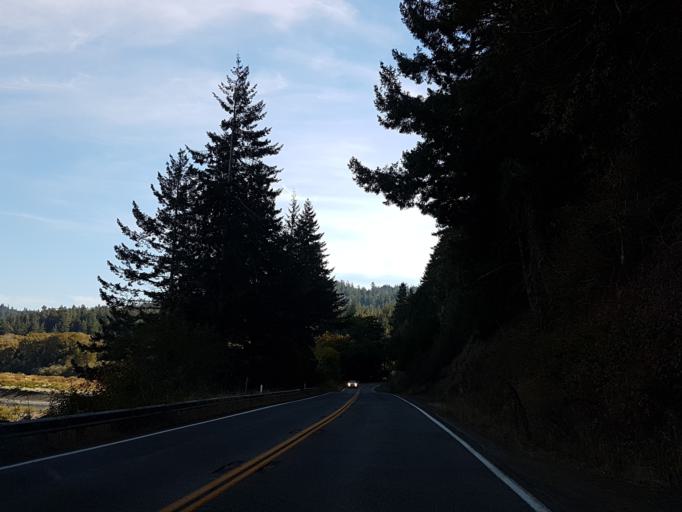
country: US
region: California
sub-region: Humboldt County
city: Rio Dell
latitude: 40.4247
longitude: -123.9799
